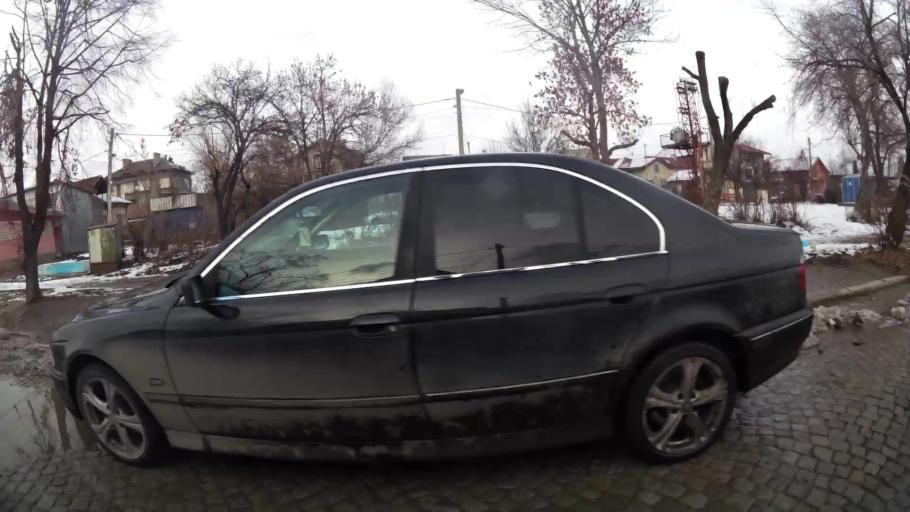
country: BG
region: Sofia-Capital
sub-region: Stolichna Obshtina
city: Sofia
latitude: 42.7219
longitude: 23.3310
